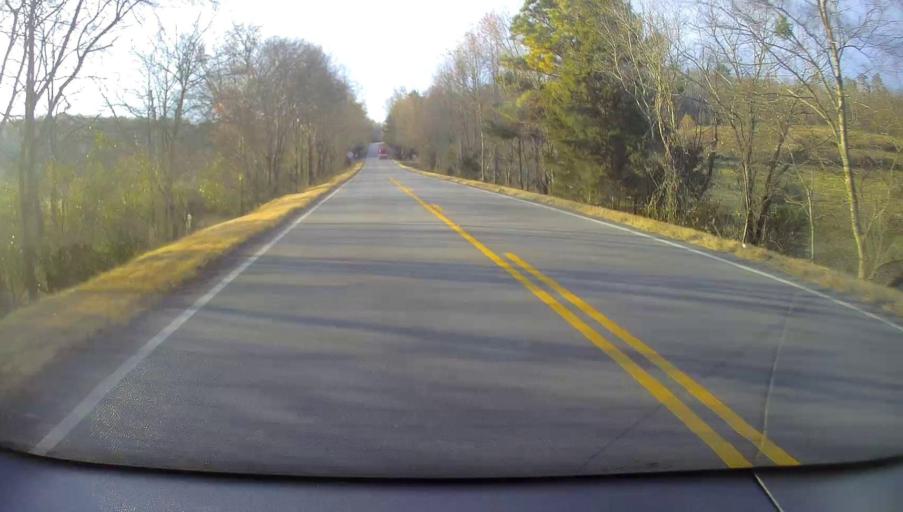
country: US
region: Alabama
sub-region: Blount County
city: Blountsville
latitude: 34.1772
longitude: -86.5124
